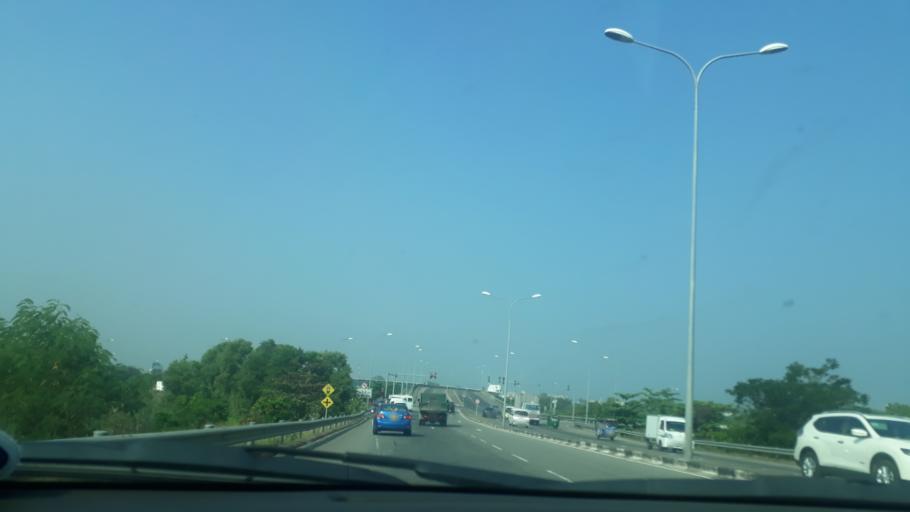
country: LK
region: Western
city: Wattala
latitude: 6.9689
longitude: 79.8958
